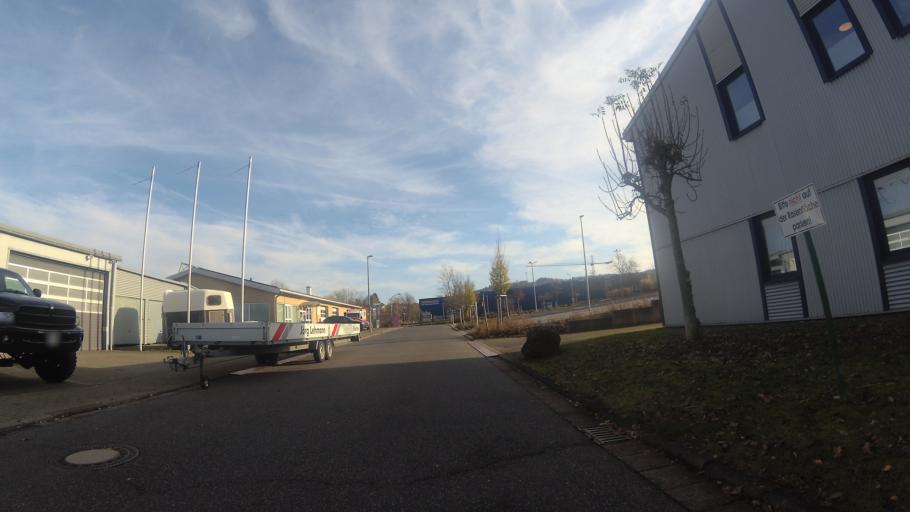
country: DE
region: Saarland
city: Freisen
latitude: 49.5511
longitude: 7.2378
